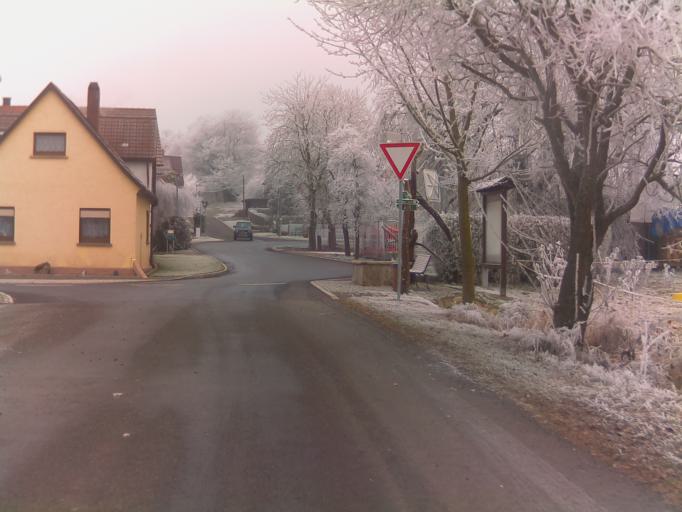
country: DE
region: Thuringia
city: Henneberg
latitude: 50.5212
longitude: 10.3227
